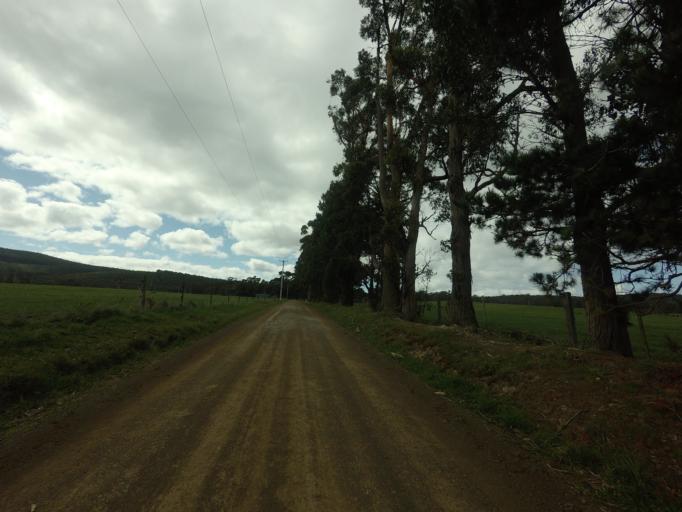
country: AU
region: Tasmania
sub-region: Huon Valley
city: Geeveston
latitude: -43.4312
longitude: 146.9904
